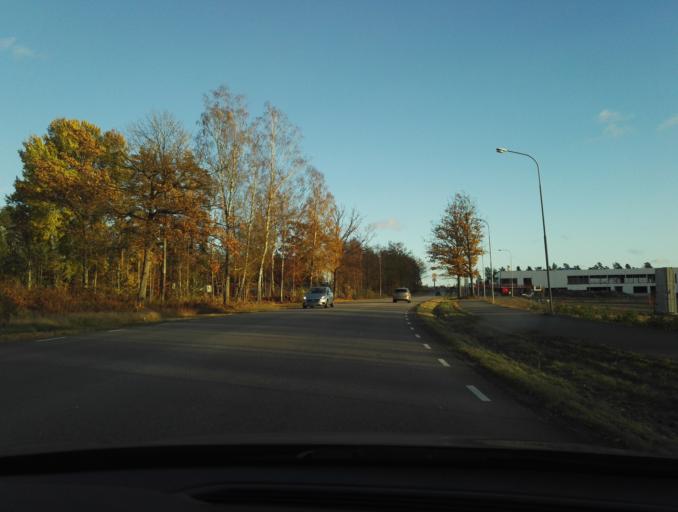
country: SE
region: Kronoberg
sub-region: Vaxjo Kommun
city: Vaexjoe
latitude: 56.8820
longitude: 14.7580
